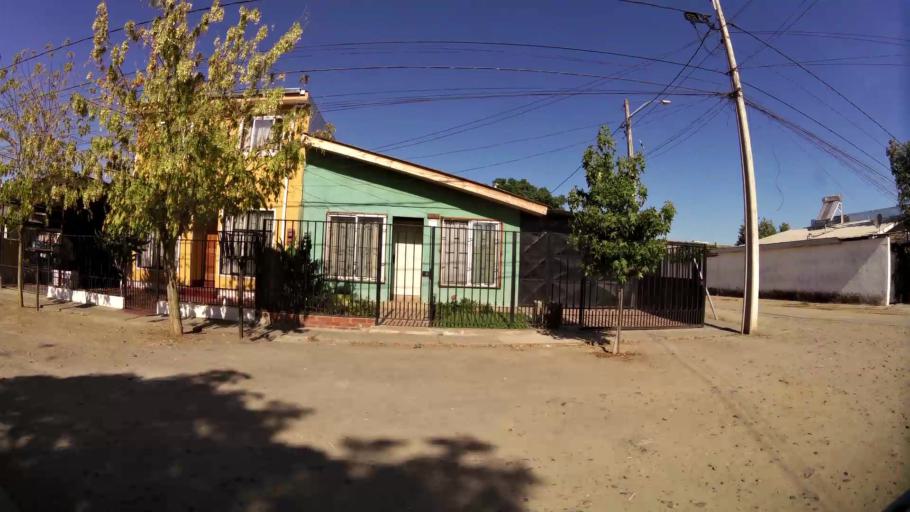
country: CL
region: Maule
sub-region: Provincia de Talca
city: Talca
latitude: -35.4442
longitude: -71.6524
